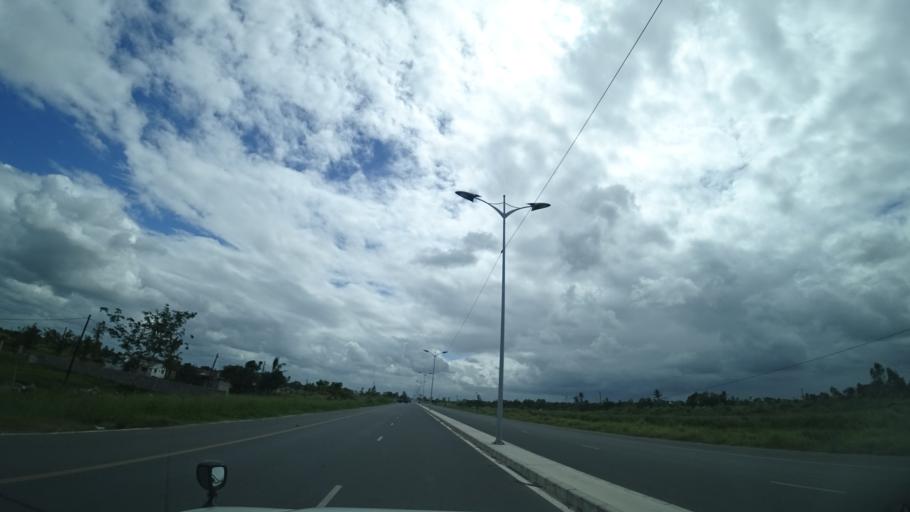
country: MZ
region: Sofala
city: Dondo
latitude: -19.6029
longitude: 34.7417
